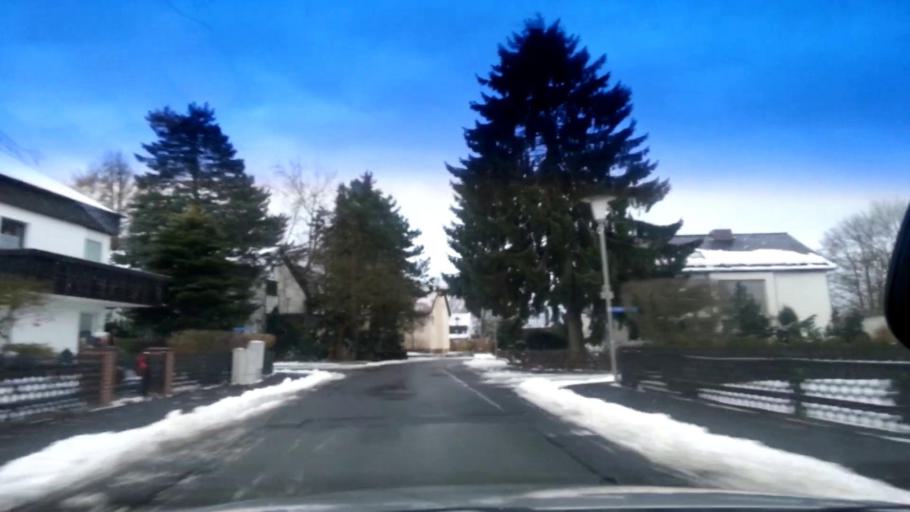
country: DE
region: Bavaria
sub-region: Upper Franconia
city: Selb
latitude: 50.1786
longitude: 12.1256
